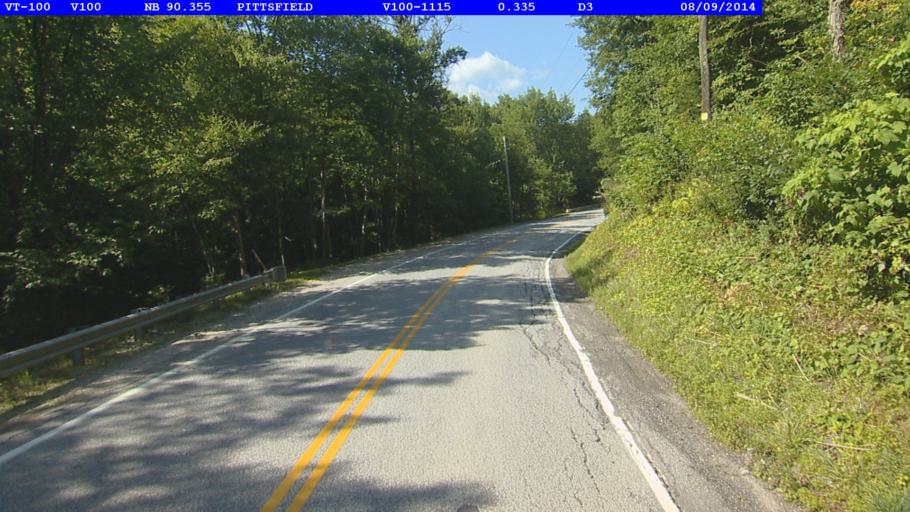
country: US
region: Vermont
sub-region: Rutland County
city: Rutland
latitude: 43.7223
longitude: -72.8228
